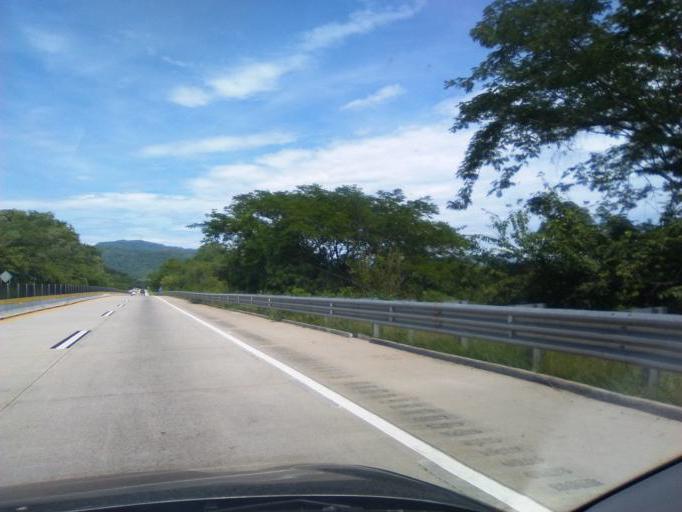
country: MX
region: Guerrero
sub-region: Acapulco de Juarez
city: Pueblo Madero (El Playon)
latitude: 17.0378
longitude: -99.6340
